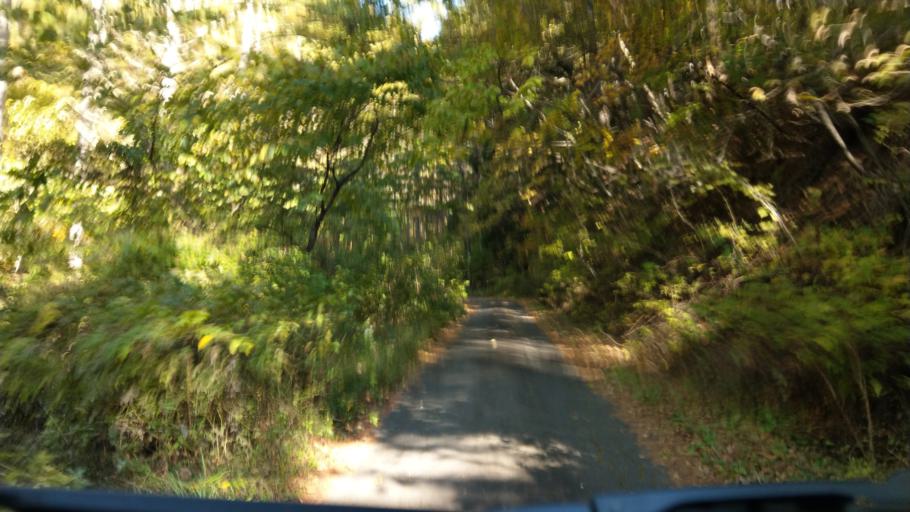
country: JP
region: Nagano
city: Komoro
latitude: 36.3745
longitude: 138.4452
